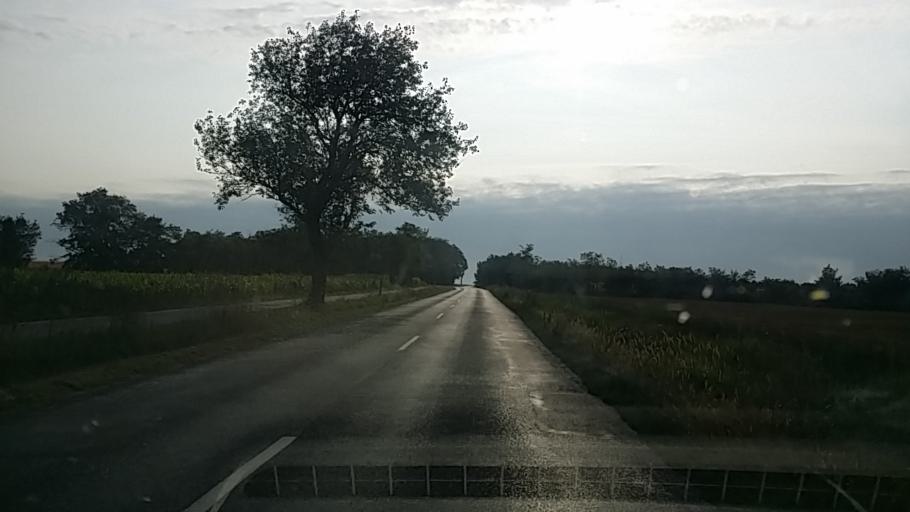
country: HU
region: Gyor-Moson-Sopron
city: Fertod
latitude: 47.6173
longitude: 16.8133
